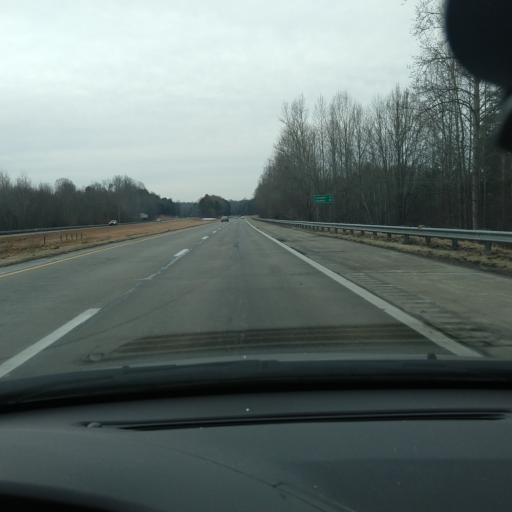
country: US
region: North Carolina
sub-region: Davidson County
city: Midway
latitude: 36.0014
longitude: -80.2374
